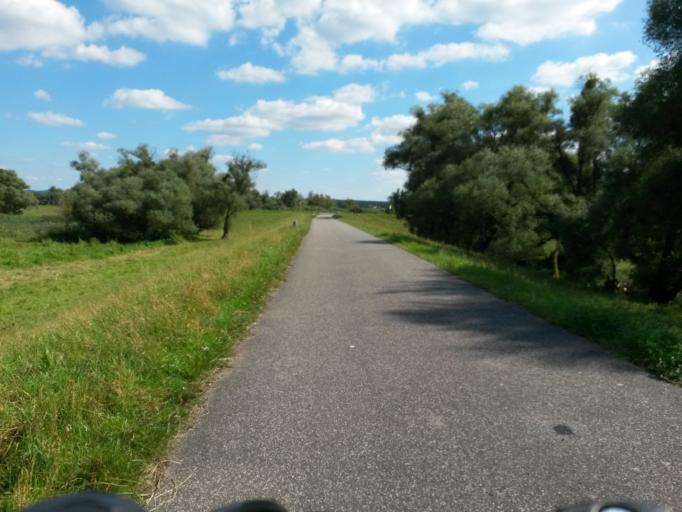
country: DE
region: Brandenburg
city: Schoneberg
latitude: 52.9878
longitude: 14.1757
